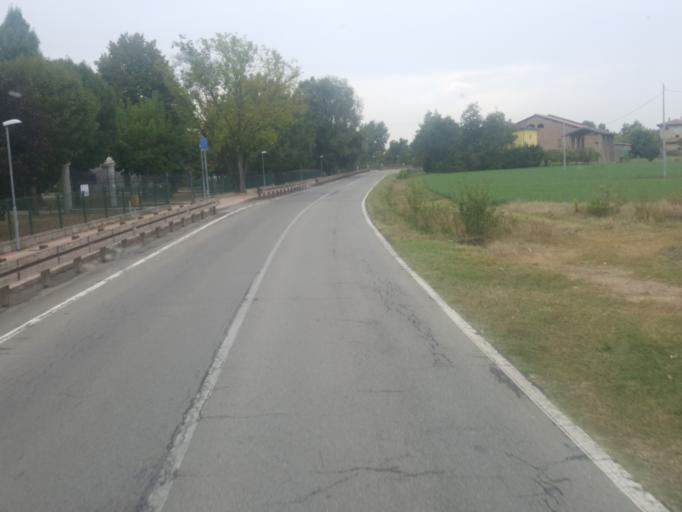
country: IT
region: Emilia-Romagna
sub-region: Provincia di Modena
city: Nonantola
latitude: 44.6752
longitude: 11.0583
